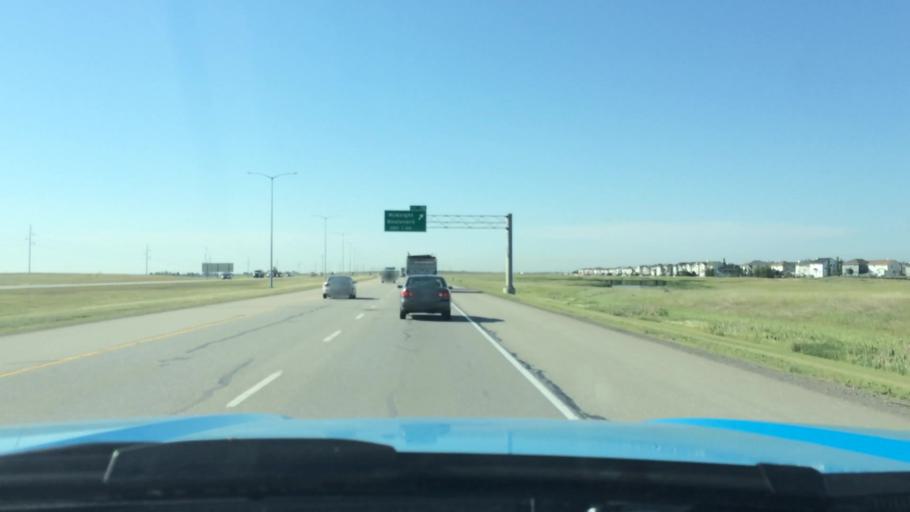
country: CA
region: Alberta
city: Chestermere
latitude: 51.1137
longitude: -113.9212
